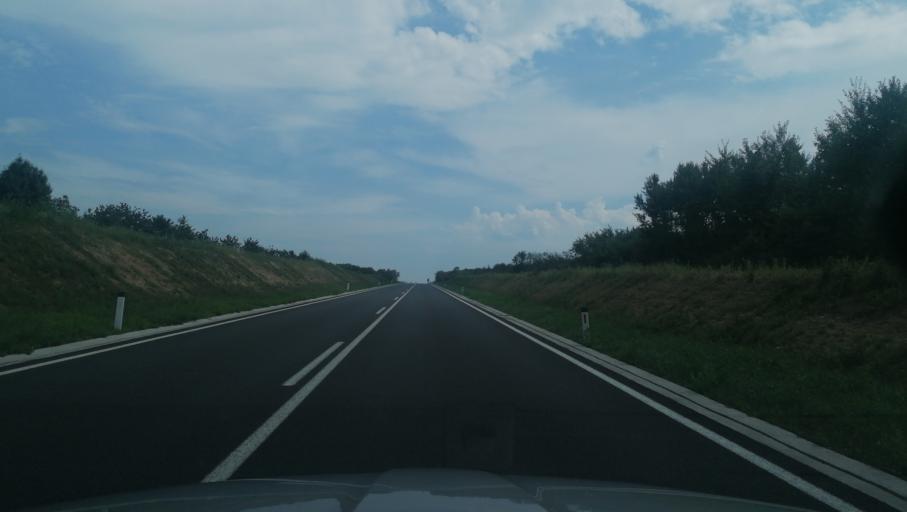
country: BA
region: Brcko
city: Brcko
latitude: 44.8321
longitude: 18.7970
